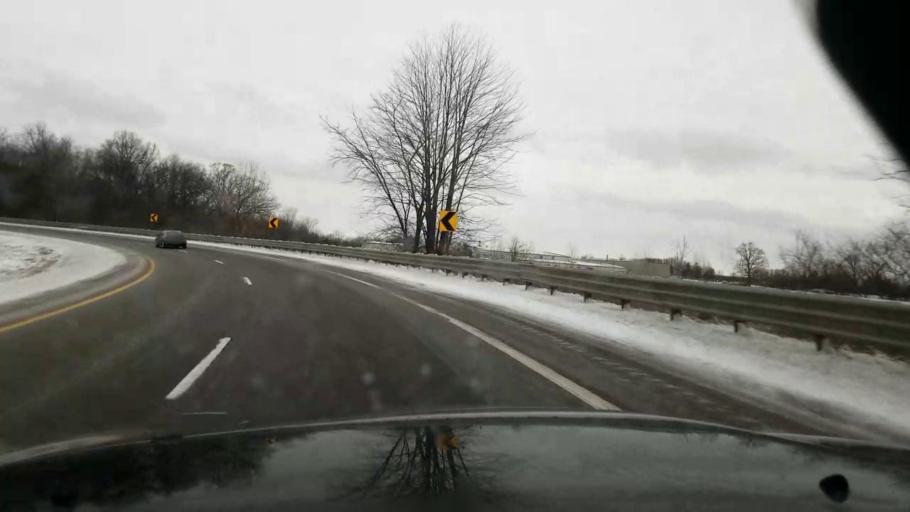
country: US
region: Michigan
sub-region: Jackson County
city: Jackson
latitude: 42.2714
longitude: -84.4753
